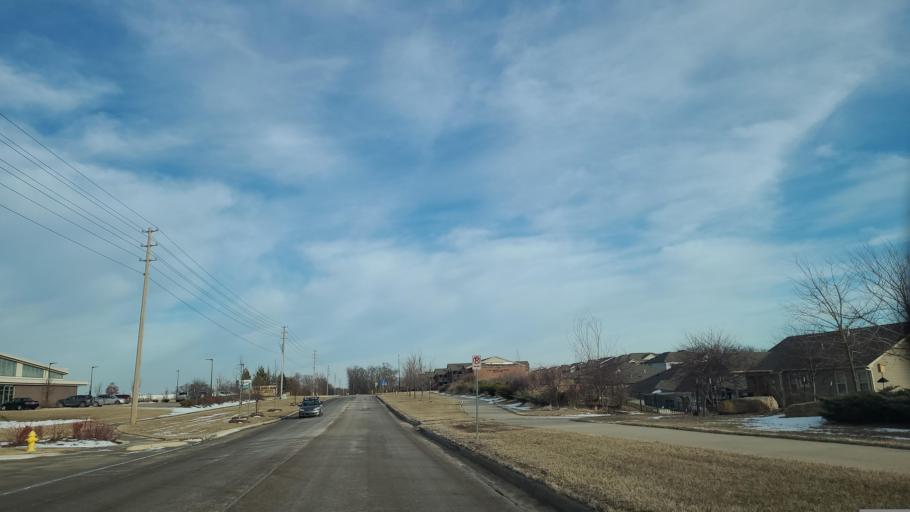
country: US
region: Kansas
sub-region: Douglas County
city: Lawrence
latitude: 38.9773
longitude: -95.3258
